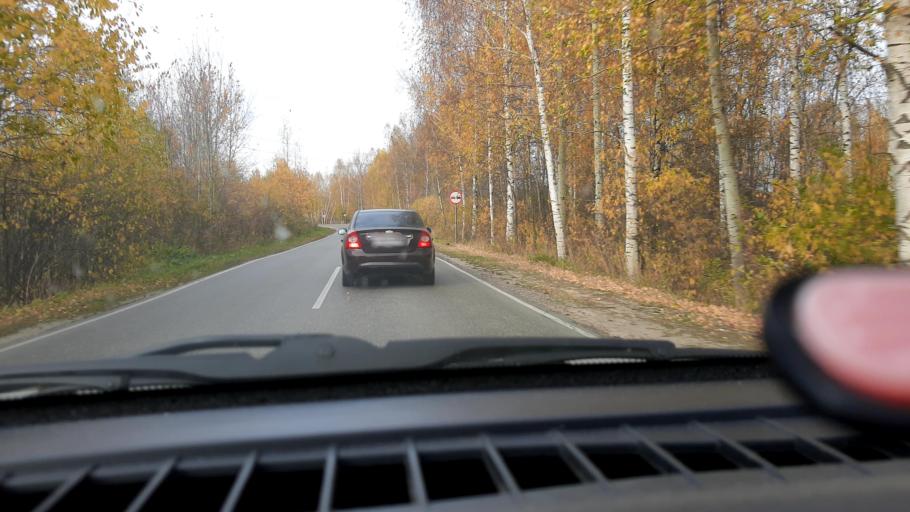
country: RU
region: Nizjnij Novgorod
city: Neklyudovo
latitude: 56.4632
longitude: 43.9002
